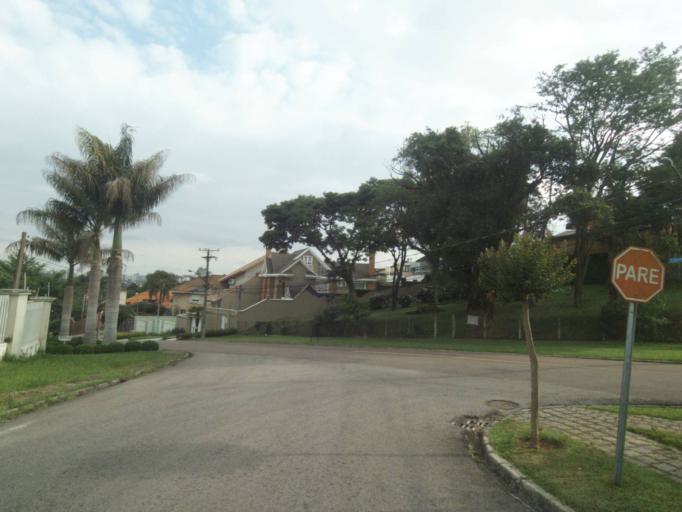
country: BR
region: Parana
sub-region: Curitiba
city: Curitiba
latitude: -25.4080
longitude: -49.3112
